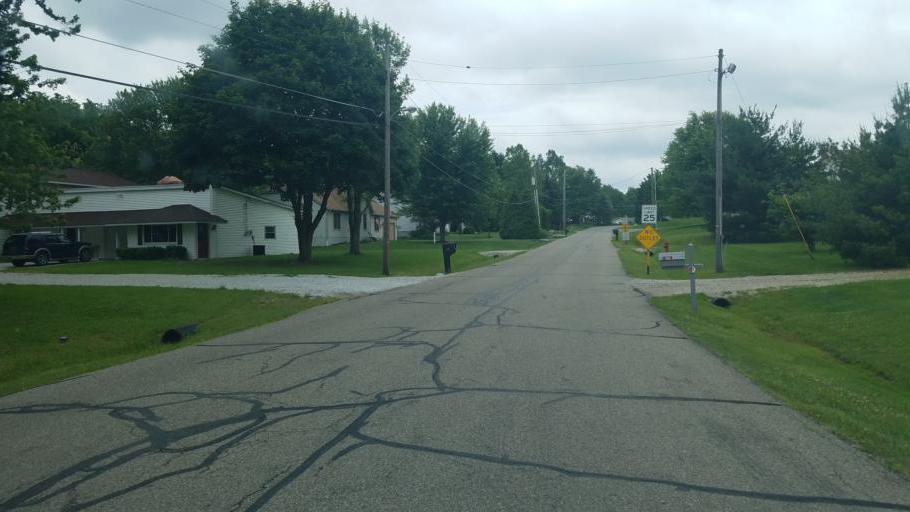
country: US
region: Ohio
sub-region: Licking County
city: Granville South
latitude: 40.0382
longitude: -82.5813
